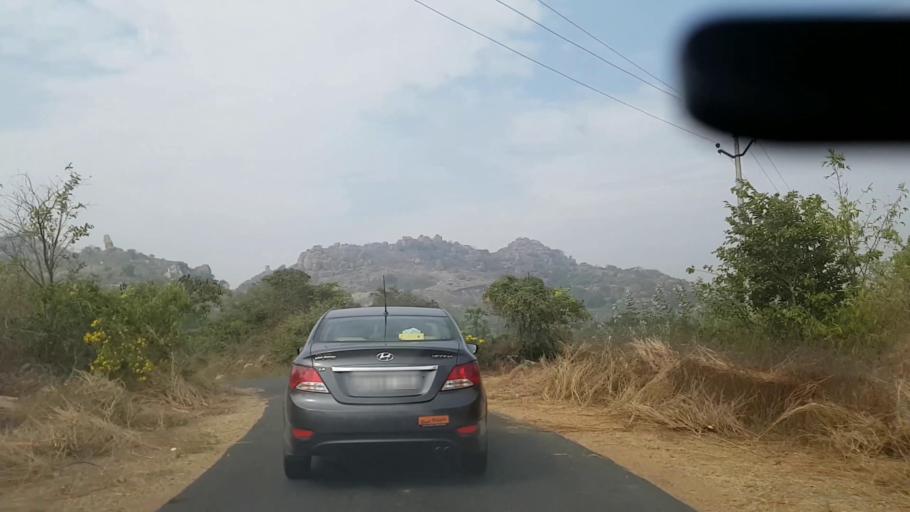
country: IN
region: Telangana
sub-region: Rangareddi
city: Ghatkesar
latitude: 17.1819
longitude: 78.8228
